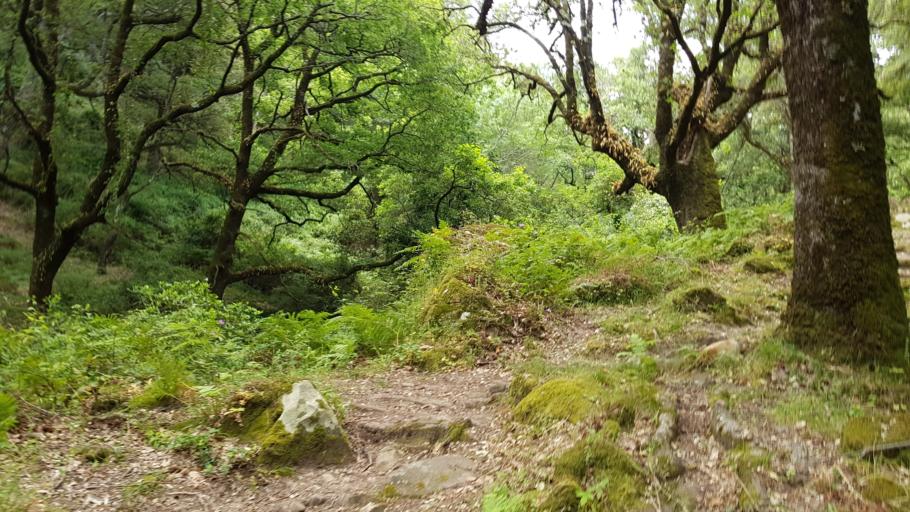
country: ES
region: Andalusia
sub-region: Provincia de Cadiz
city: Alcala de los Gazules
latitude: 36.5185
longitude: -5.5935
